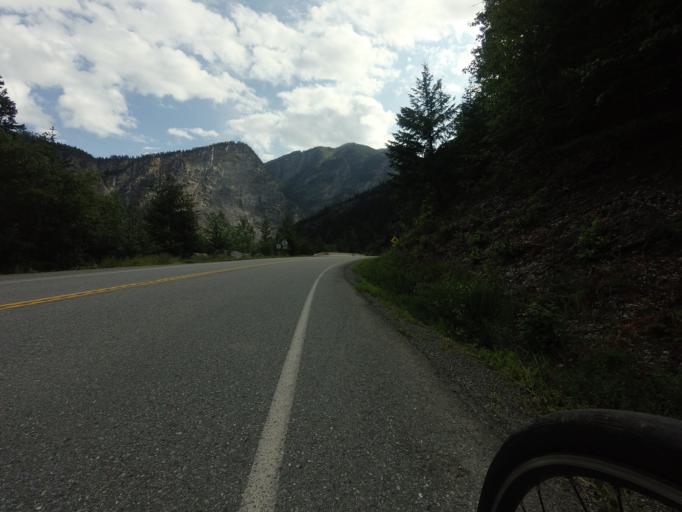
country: CA
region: British Columbia
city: Lillooet
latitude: 50.6400
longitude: -122.0735
